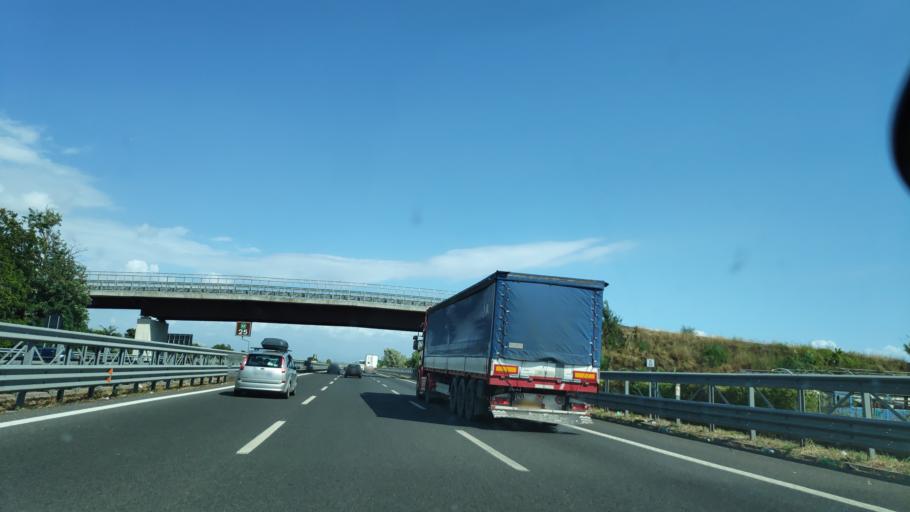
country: IT
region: Campania
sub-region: Provincia di Salerno
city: Pontecagnano
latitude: 40.6463
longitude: 14.8876
